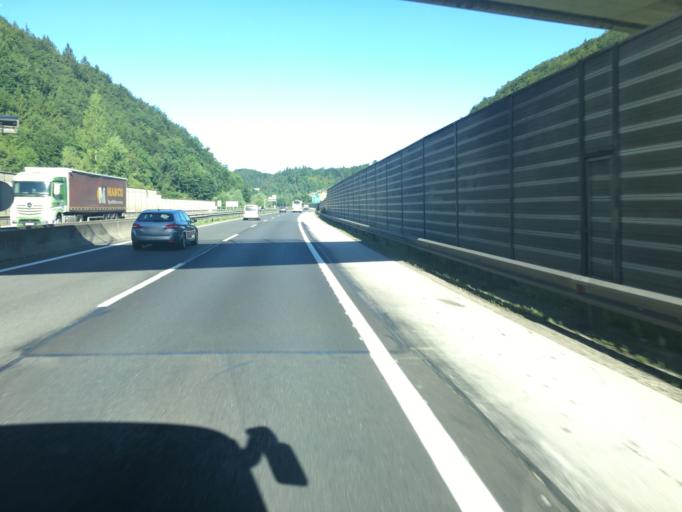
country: SI
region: Lukovica
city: Lukovica pri Domzalah
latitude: 46.1709
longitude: 14.7142
